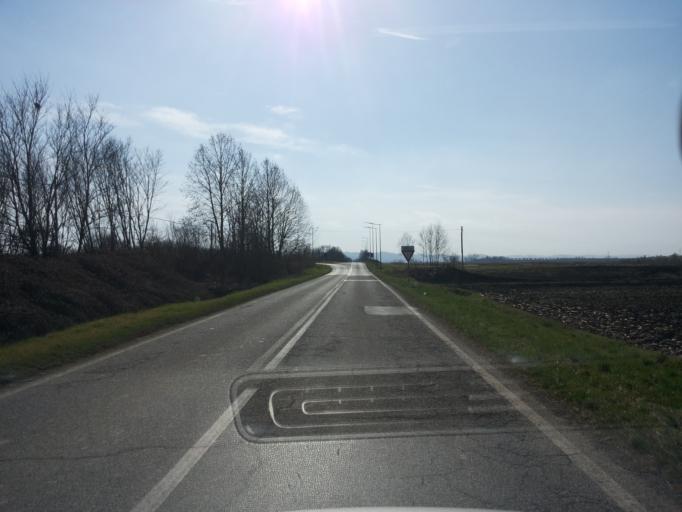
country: IT
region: Piedmont
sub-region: Provincia di Vercelli
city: Tricerro
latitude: 45.2269
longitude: 8.3161
